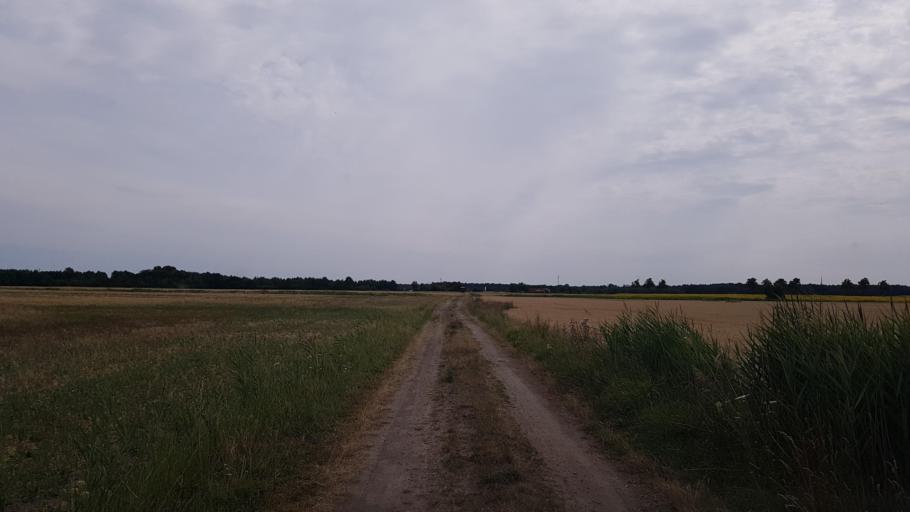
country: DE
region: Brandenburg
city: Bronkow
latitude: 51.5952
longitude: 13.9339
